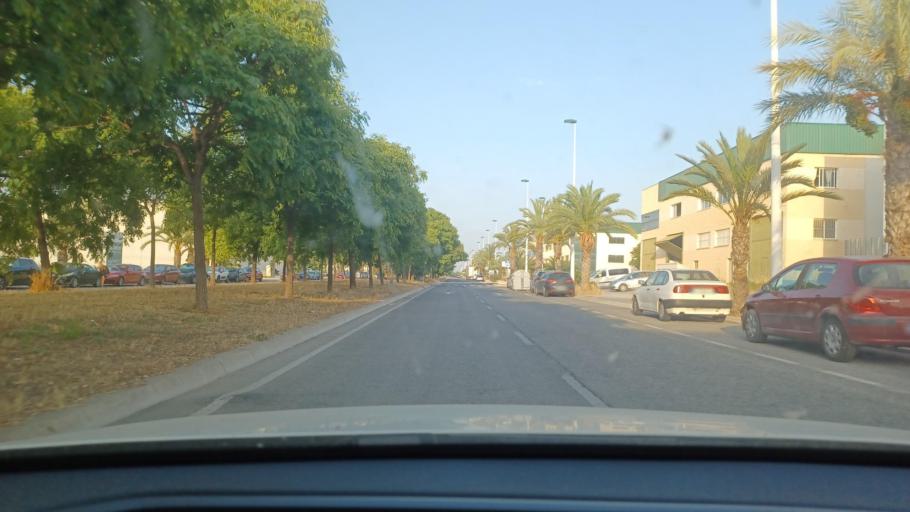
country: ES
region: Valencia
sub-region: Provincia de Alicante
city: Elche
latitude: 38.2890
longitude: -0.6184
